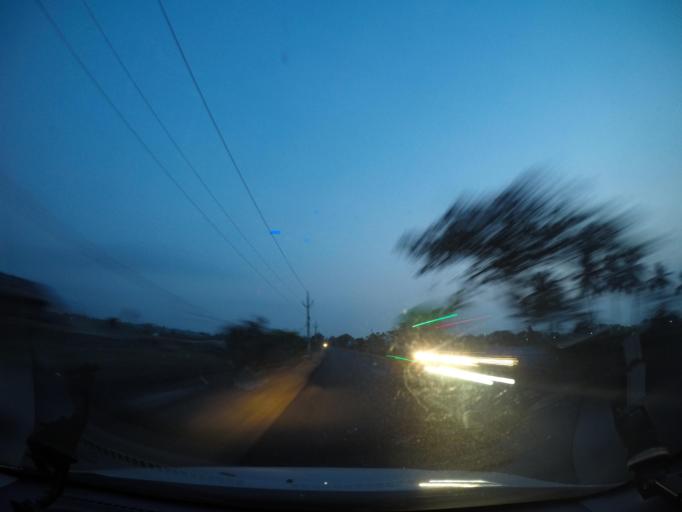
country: IN
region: Andhra Pradesh
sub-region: West Godavari
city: Tadepallegudem
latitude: 16.7757
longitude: 81.4240
